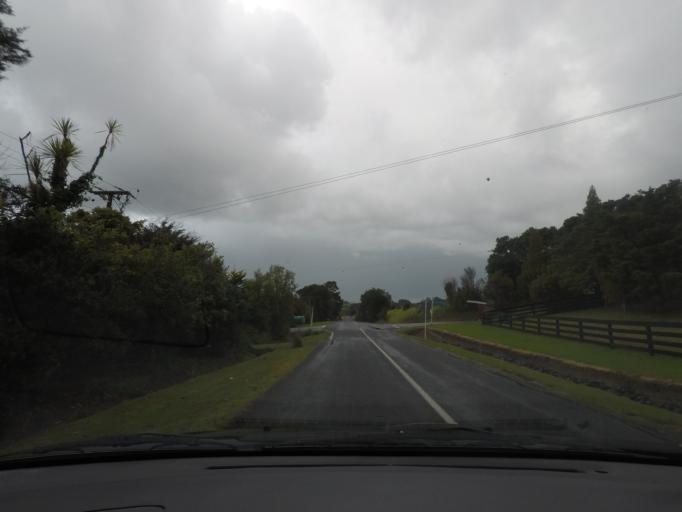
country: NZ
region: Auckland
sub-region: Auckland
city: Warkworth
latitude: -36.4724
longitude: 174.7342
